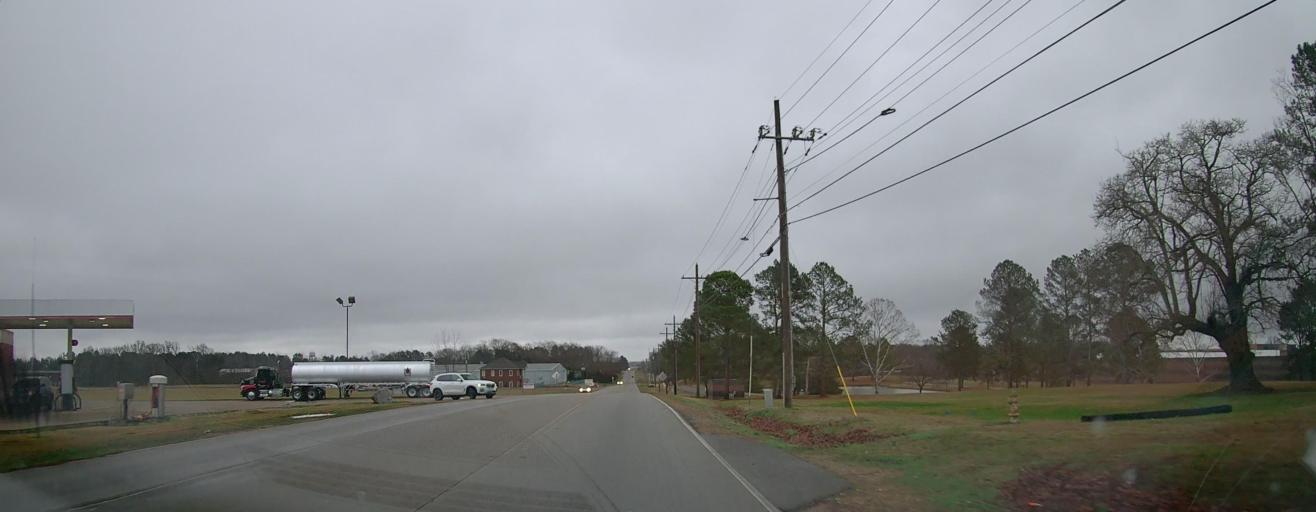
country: US
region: Mississippi
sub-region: Alcorn County
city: Corinth
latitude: 34.9089
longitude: -88.5417
